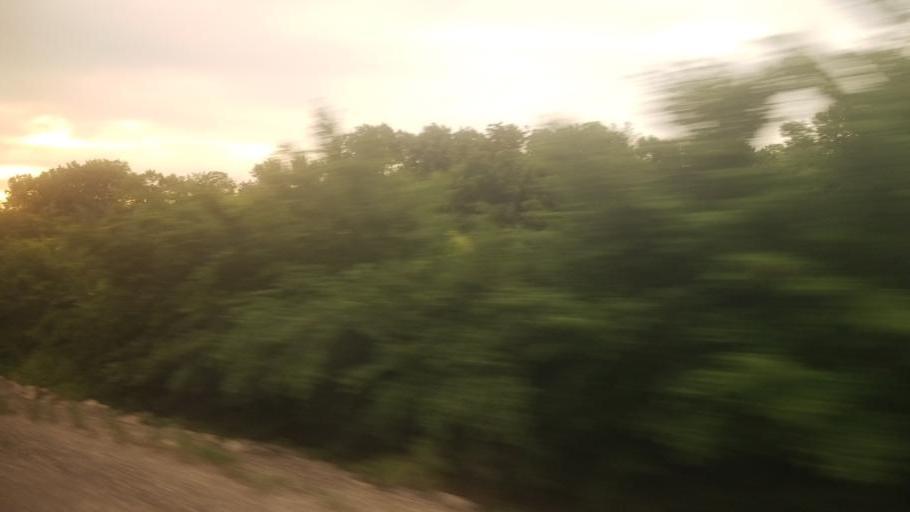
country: US
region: Kansas
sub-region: Chase County
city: Cottonwood Falls
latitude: 38.3909
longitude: -96.6290
